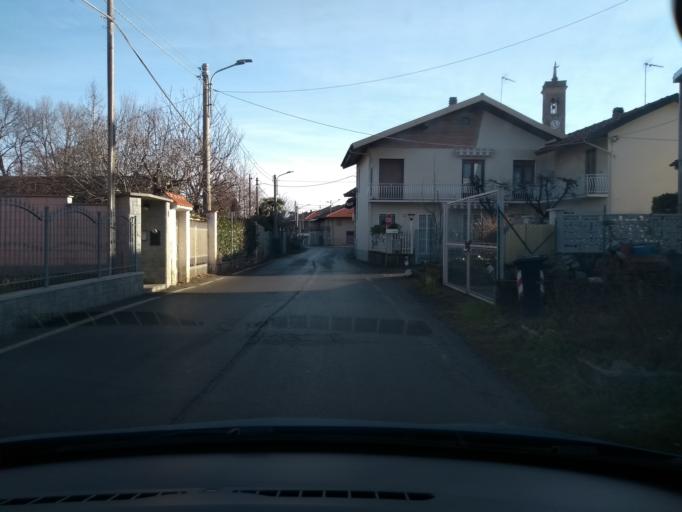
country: IT
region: Piedmont
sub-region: Provincia di Torino
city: Barbania
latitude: 45.2845
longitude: 7.6397
